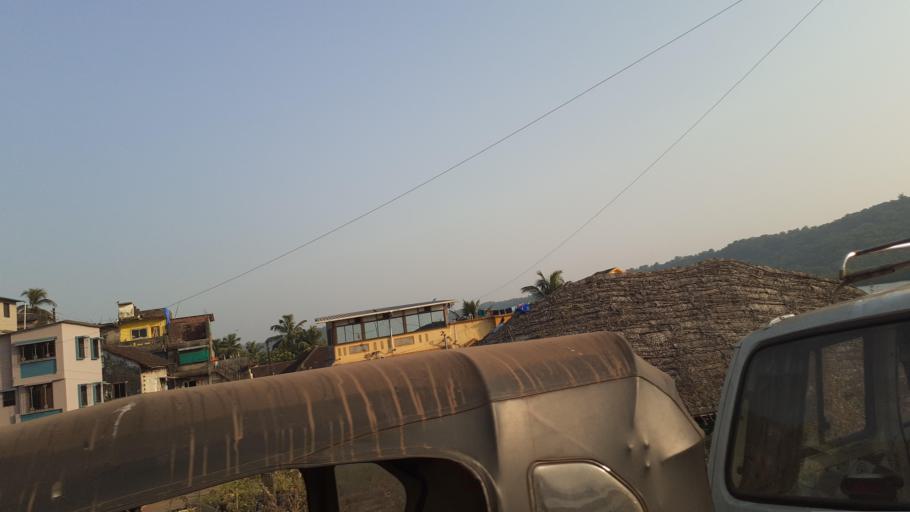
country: IN
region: Maharashtra
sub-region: Ratnagiri
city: Ratnagiri
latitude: 17.0416
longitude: 73.2975
